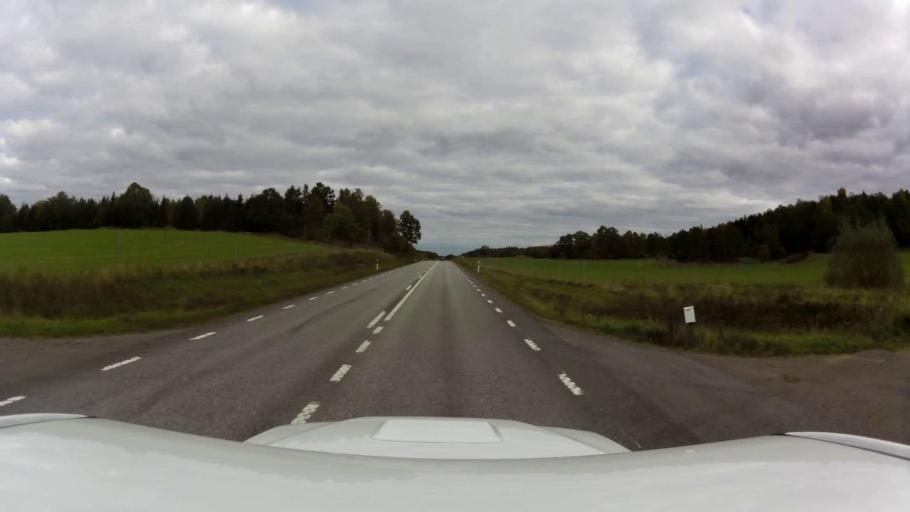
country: SE
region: OEstergoetland
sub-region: Kinda Kommun
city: Rimforsa
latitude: 58.1922
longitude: 15.6667
